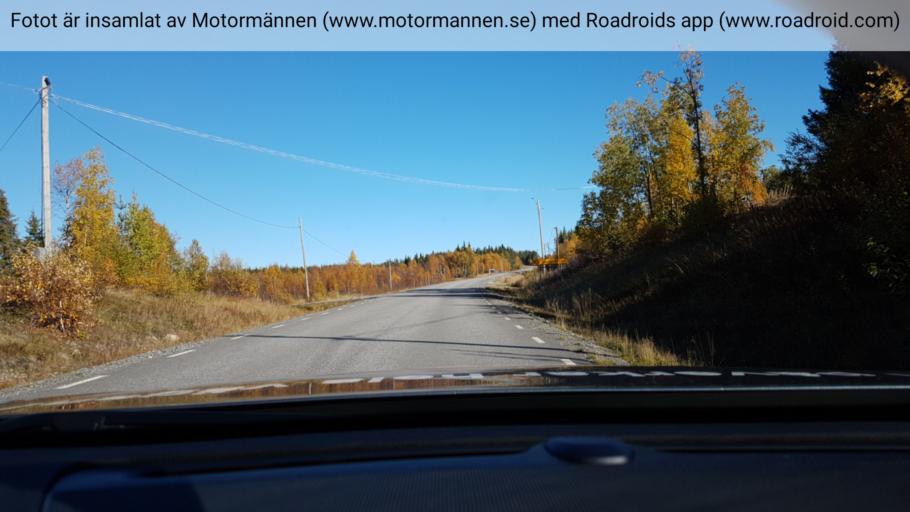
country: SE
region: Norrbotten
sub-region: Gallivare Kommun
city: Gaellivare
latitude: 66.7651
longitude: 21.0335
